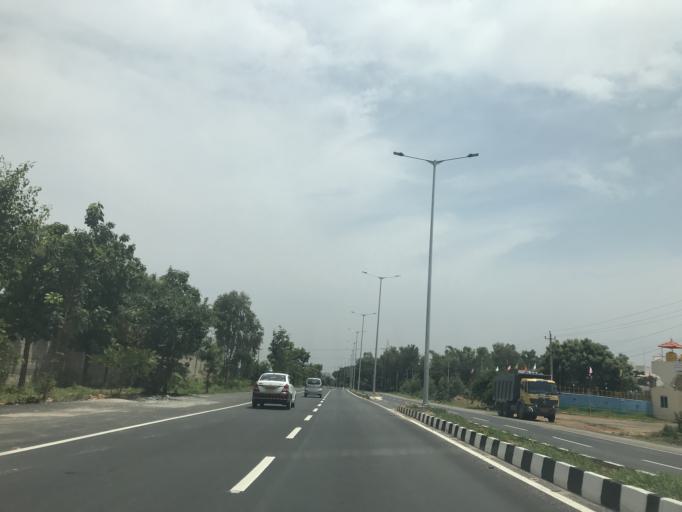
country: IN
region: Karnataka
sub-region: Bangalore Urban
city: Yelahanka
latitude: 13.1507
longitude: 77.6760
